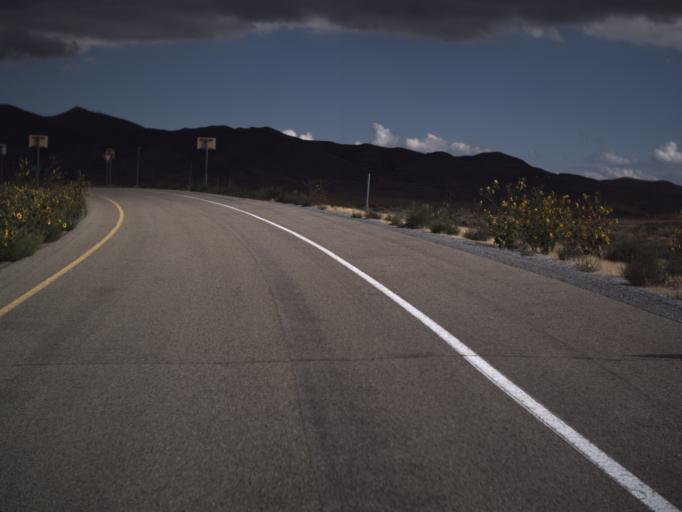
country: US
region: Utah
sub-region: Tooele County
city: Grantsville
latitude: 40.8205
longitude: -112.9047
